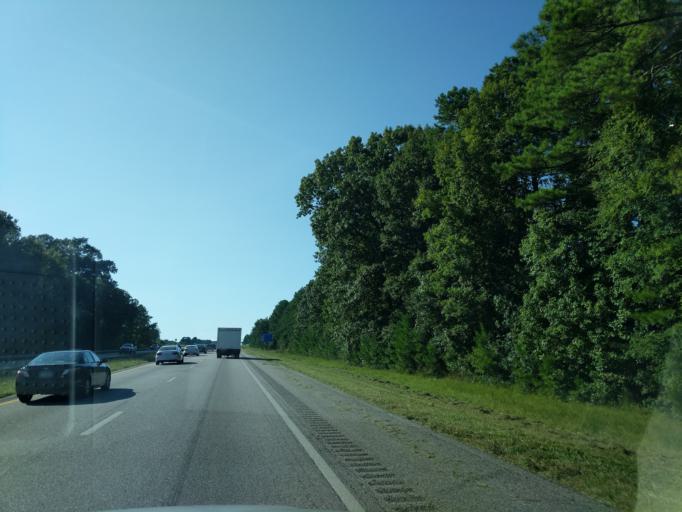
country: US
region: South Carolina
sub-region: Laurens County
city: Clinton
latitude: 34.5015
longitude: -81.8505
